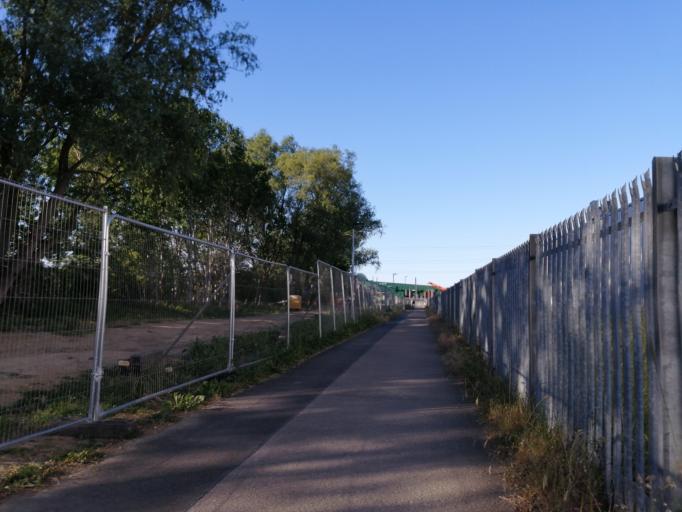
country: GB
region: England
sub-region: Peterborough
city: Marholm
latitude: 52.6082
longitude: -0.2854
